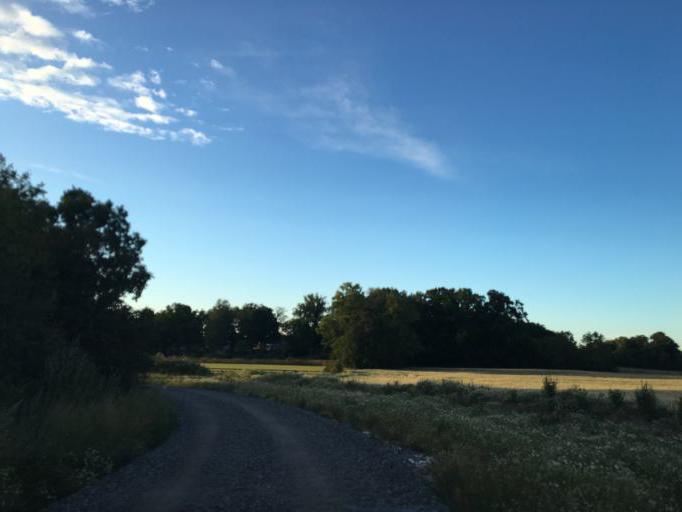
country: SE
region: Soedermanland
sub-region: Eskilstuna Kommun
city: Torshalla
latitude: 59.4322
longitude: 16.4355
